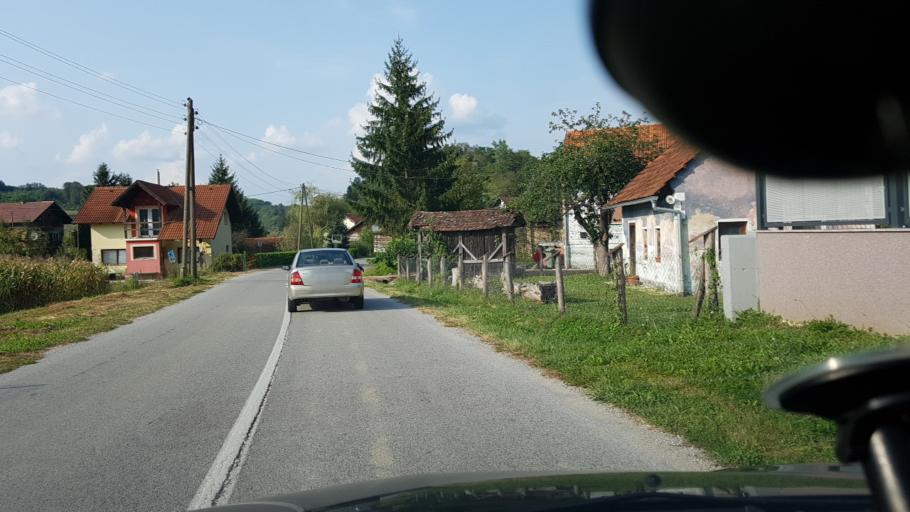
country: SI
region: Bistrica ob Sotli
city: Bistrica ob Sotli
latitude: 46.0322
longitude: 15.7731
